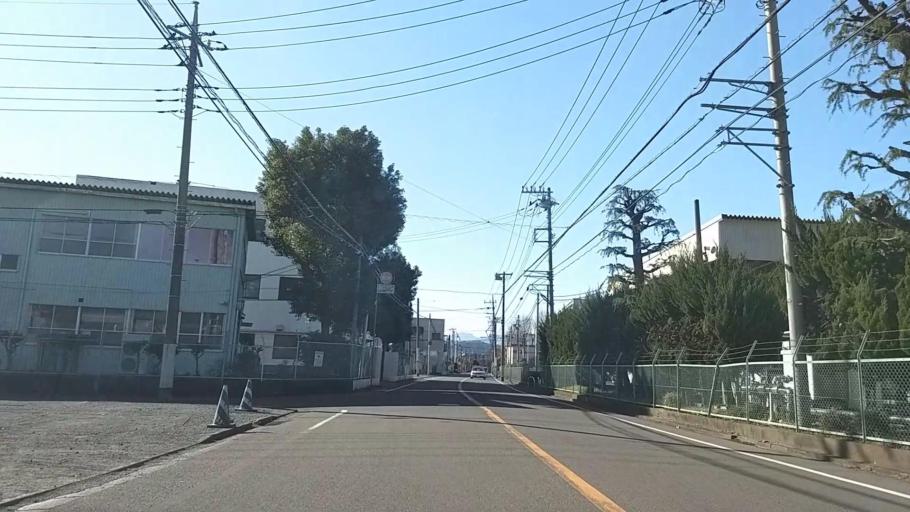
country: JP
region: Kanagawa
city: Hadano
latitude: 35.3838
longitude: 139.2068
